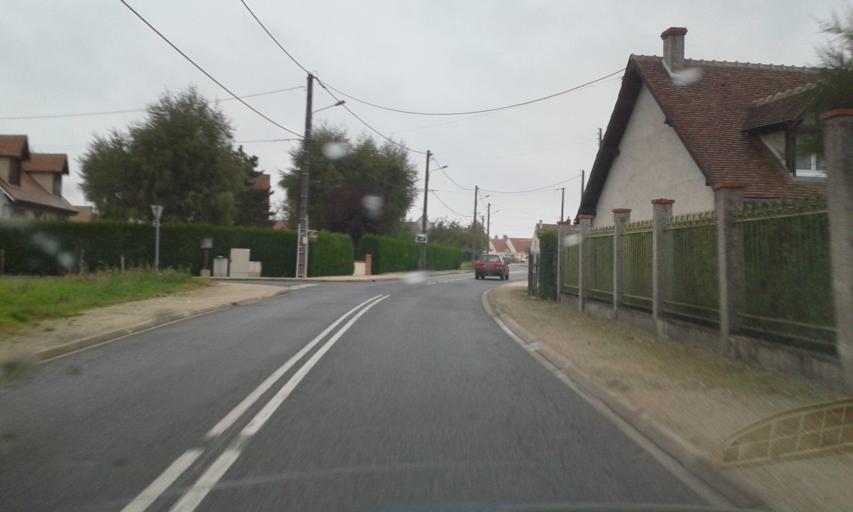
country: FR
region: Centre
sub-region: Departement du Loiret
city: Olivet
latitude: 47.8448
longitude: 1.8809
